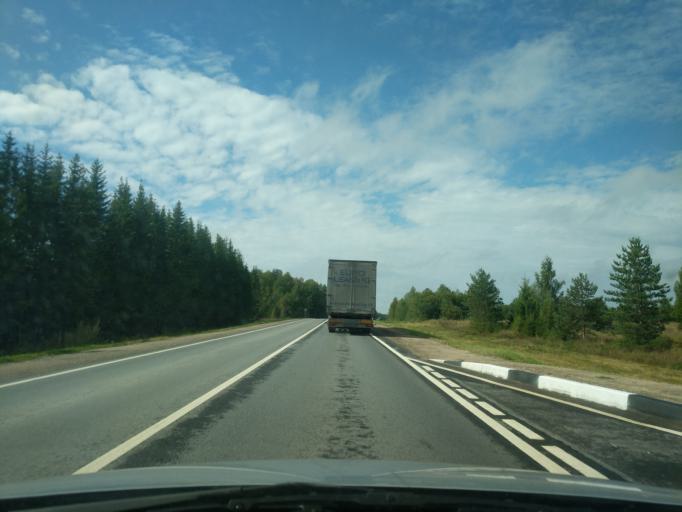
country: RU
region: Kostroma
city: Sudislavl'
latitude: 57.8453
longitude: 41.8236
